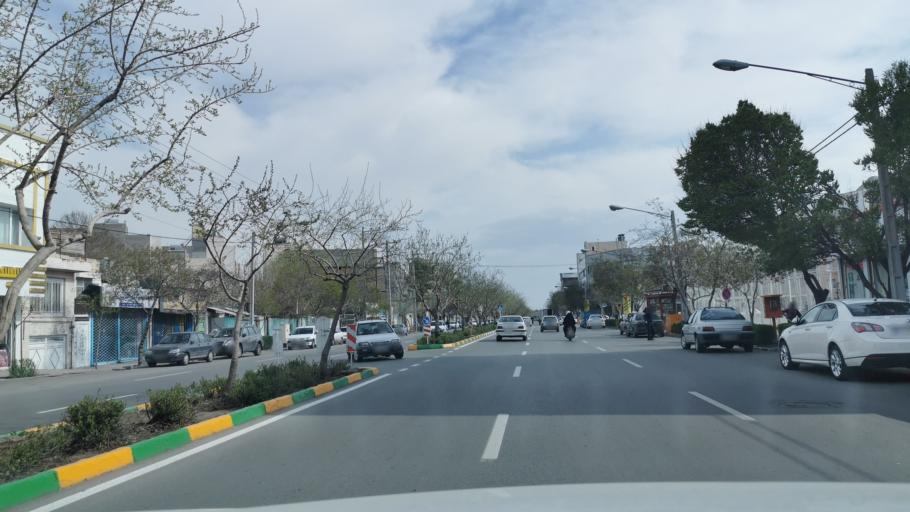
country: IR
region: Razavi Khorasan
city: Mashhad
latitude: 36.3160
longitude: 59.6095
